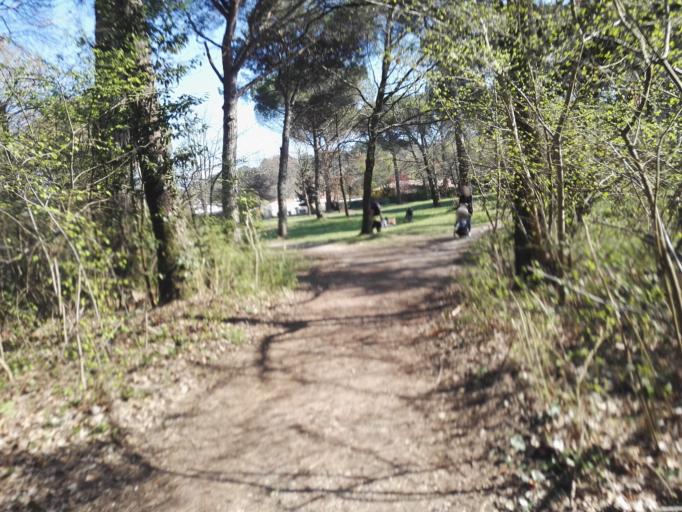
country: FR
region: Aquitaine
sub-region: Departement de la Gironde
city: Gradignan
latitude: 44.7683
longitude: -0.6057
